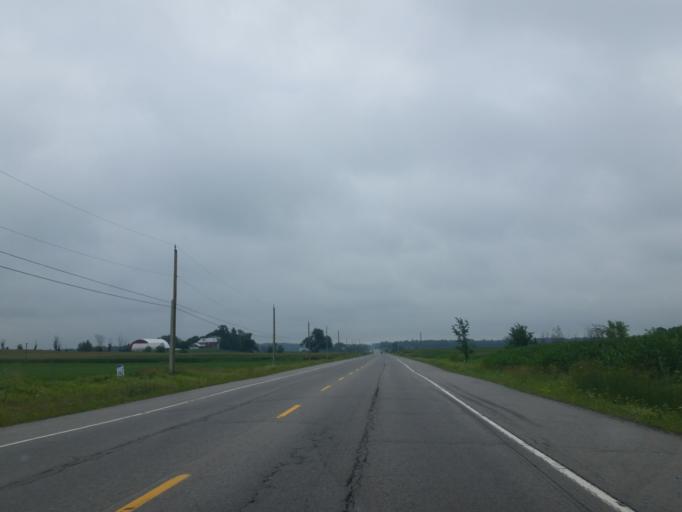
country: CA
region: Ontario
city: Clarence-Rockland
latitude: 45.4072
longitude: -75.4001
